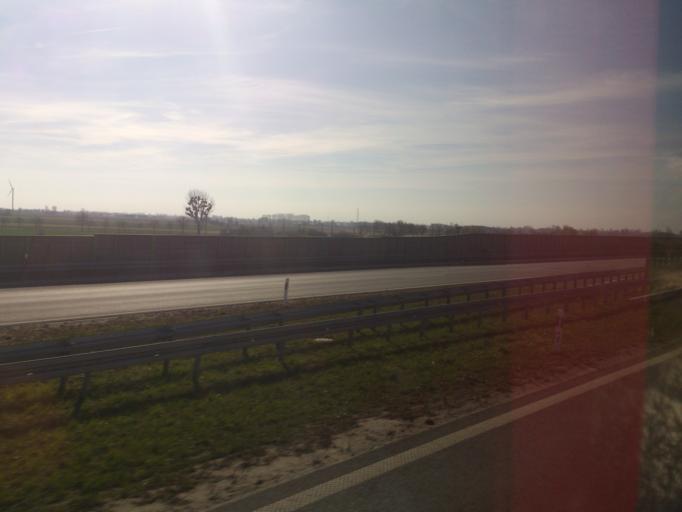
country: PL
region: Kujawsko-Pomorskie
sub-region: Powiat aleksandrowski
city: Raciazek
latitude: 52.8274
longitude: 18.8028
